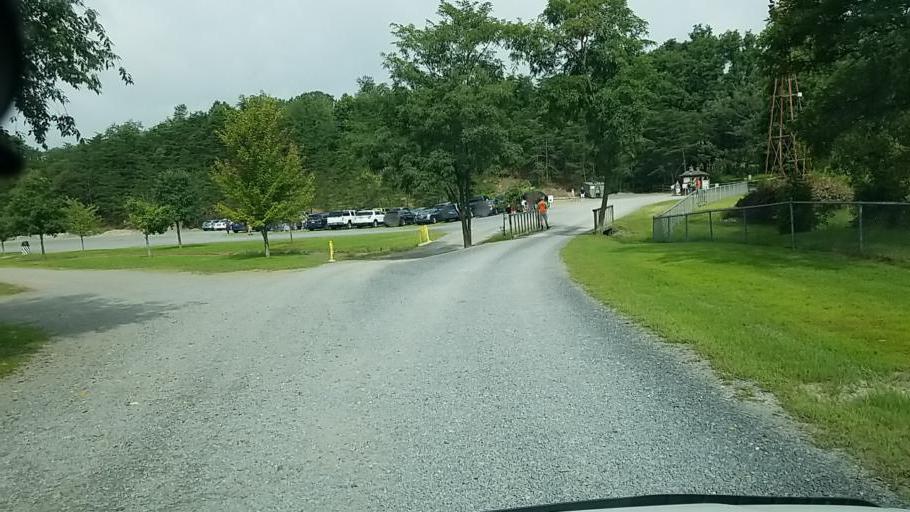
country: US
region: Pennsylvania
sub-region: Dauphin County
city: Matamoras
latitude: 40.5000
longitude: -76.8949
